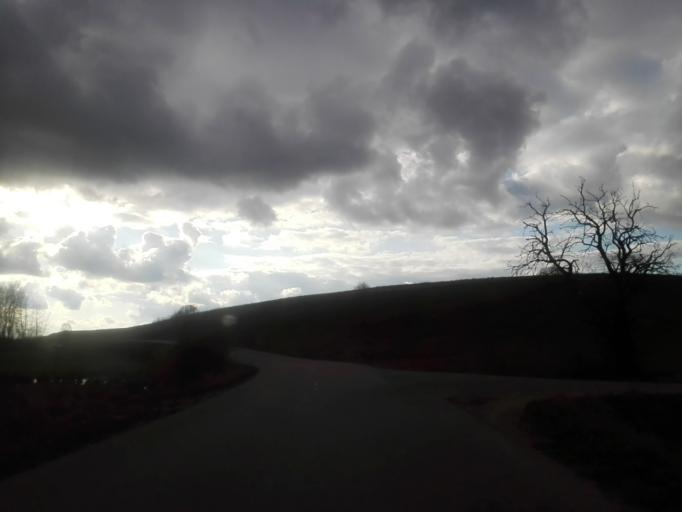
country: PL
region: Podlasie
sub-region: Suwalki
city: Suwalki
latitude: 54.2010
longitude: 22.9887
